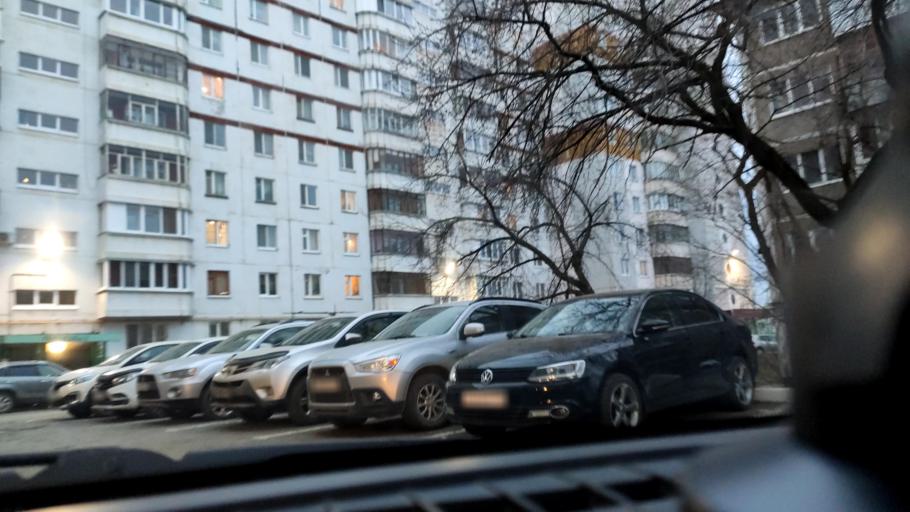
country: RU
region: Perm
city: Perm
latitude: 57.9966
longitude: 56.2373
